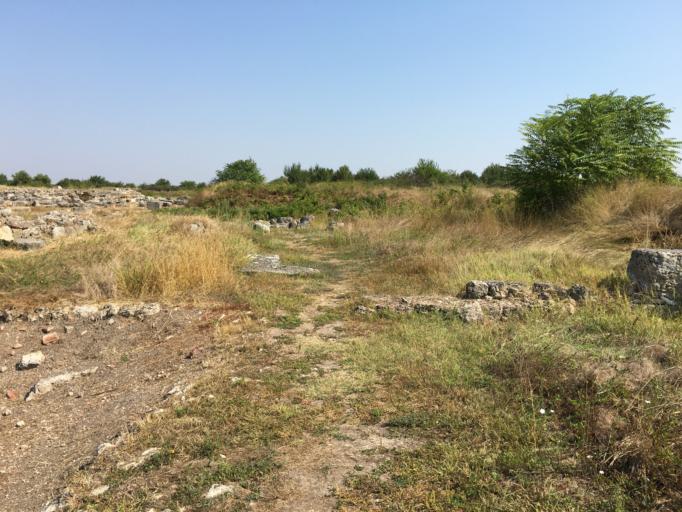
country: RO
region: Olt
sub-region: Oras Corabia
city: Corabia
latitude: 43.7093
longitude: 24.4658
